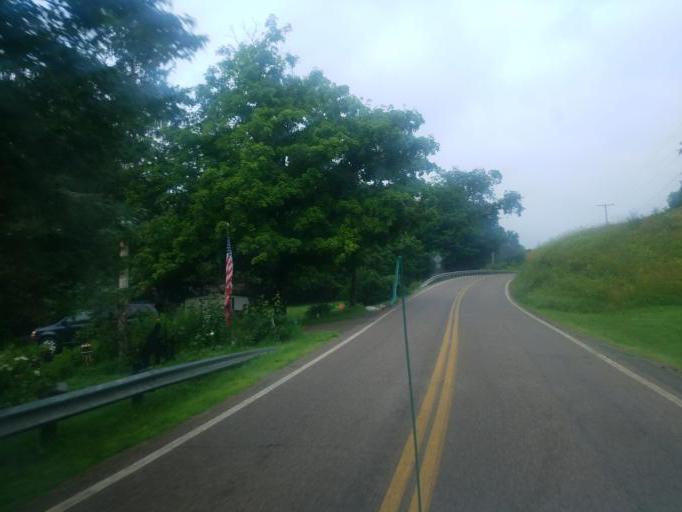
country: US
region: Ohio
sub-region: Columbiana County
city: Salineville
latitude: 40.5739
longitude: -80.9347
